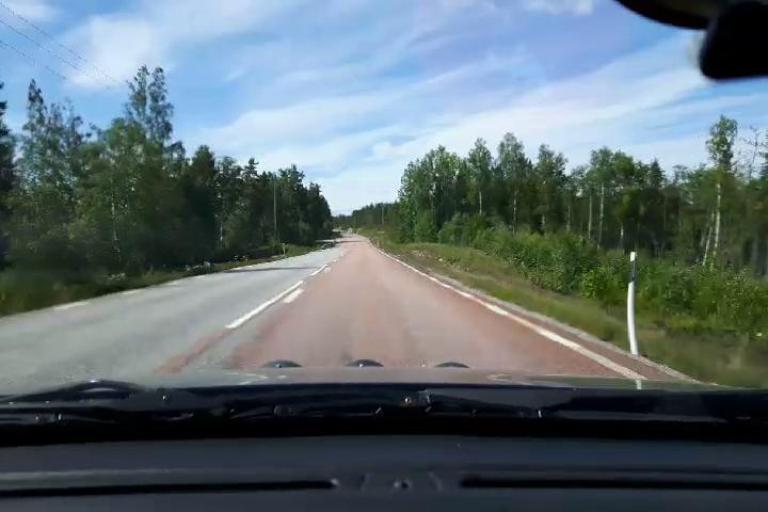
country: SE
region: Gaevleborg
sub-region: Soderhamns Kommun
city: Soderhamn
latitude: 61.1264
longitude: 16.9304
